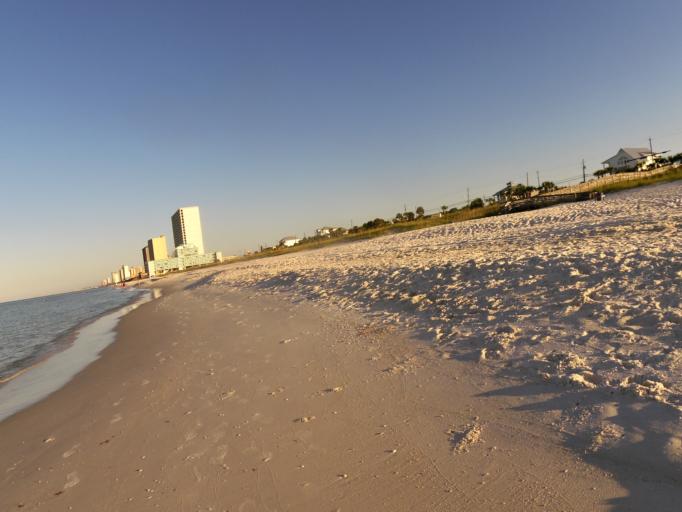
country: US
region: Florida
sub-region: Bay County
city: Panama City Beach
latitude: 30.2003
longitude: -85.8507
